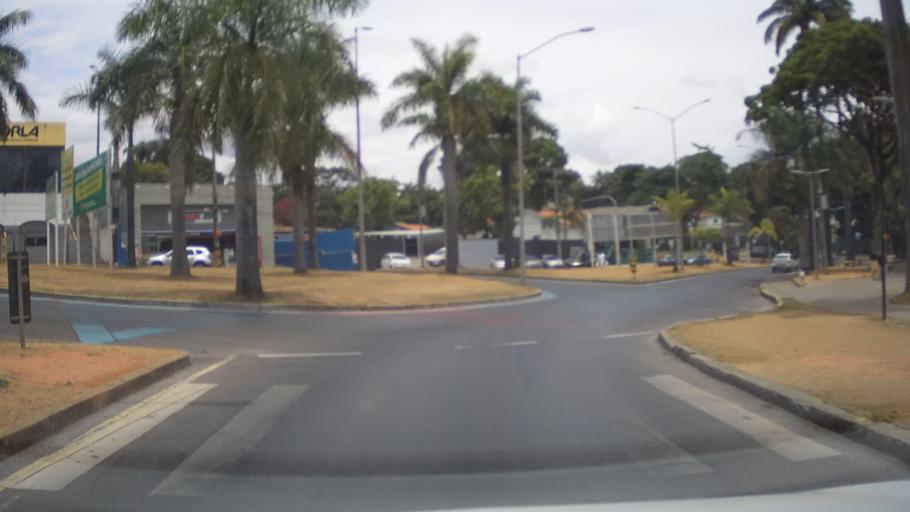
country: BR
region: Minas Gerais
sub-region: Belo Horizonte
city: Belo Horizonte
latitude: -19.8540
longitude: -43.9685
